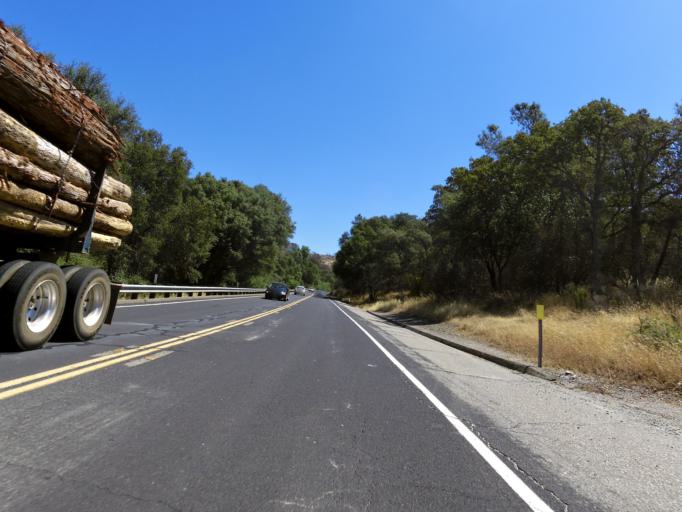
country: US
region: California
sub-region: Mariposa County
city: Mariposa
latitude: 37.4829
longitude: -120.0059
